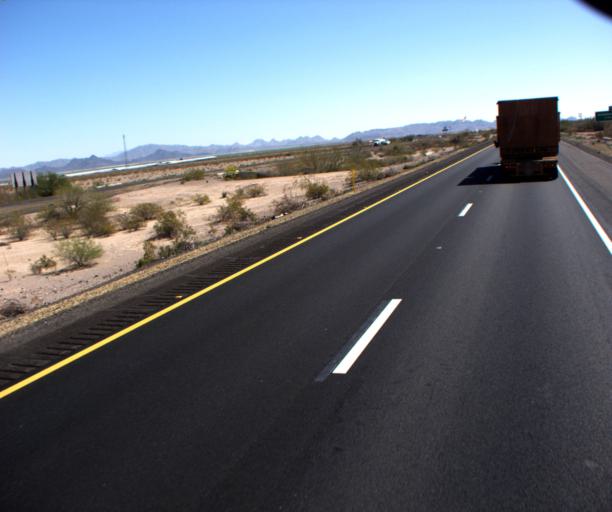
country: US
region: Arizona
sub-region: La Paz County
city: Salome
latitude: 33.6337
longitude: -113.7882
